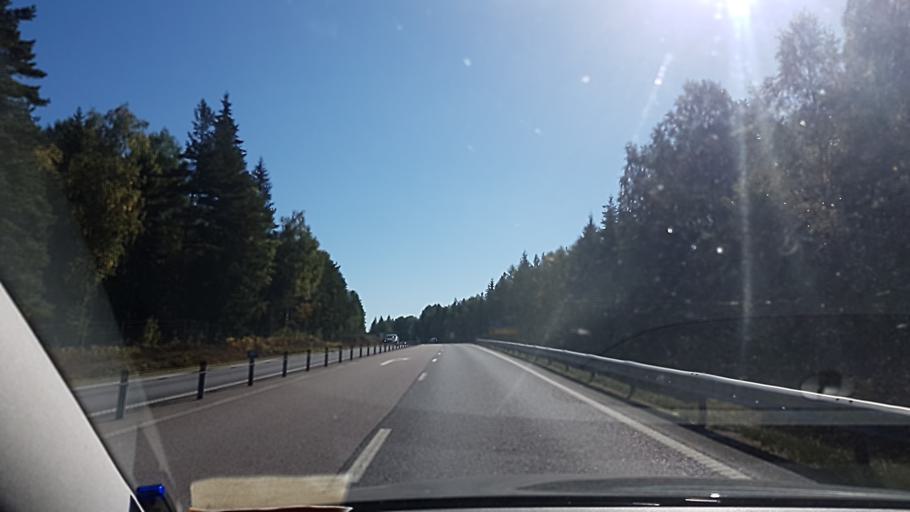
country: SE
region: Kronoberg
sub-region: Vaxjo Kommun
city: Ingelstad
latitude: 56.8731
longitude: 14.9366
